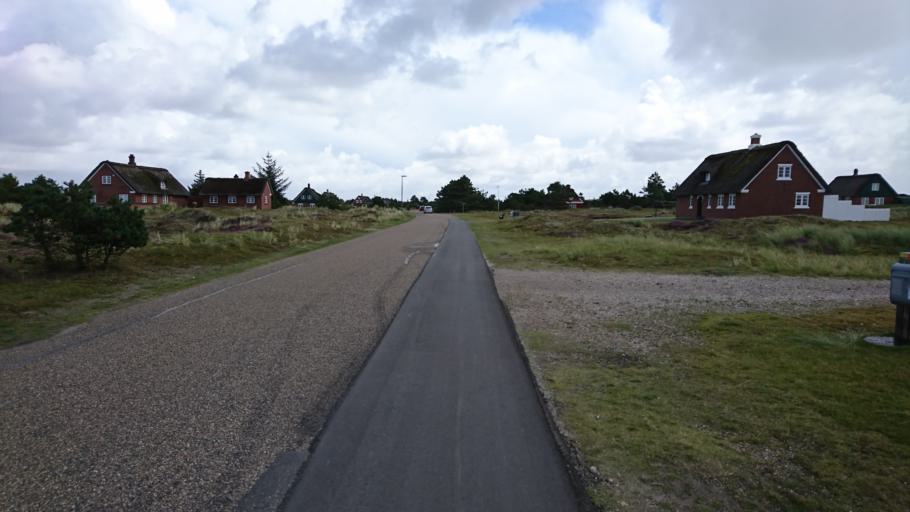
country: DK
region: South Denmark
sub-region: Fano Kommune
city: Nordby
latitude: 55.3482
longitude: 8.4522
